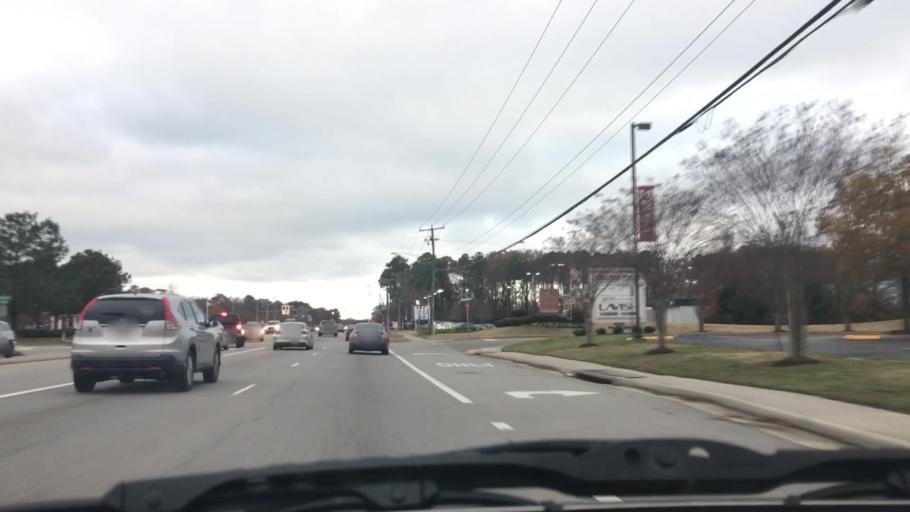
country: US
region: Virginia
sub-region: City of Virginia Beach
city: Virginia Beach
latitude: 36.8220
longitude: -76.1241
